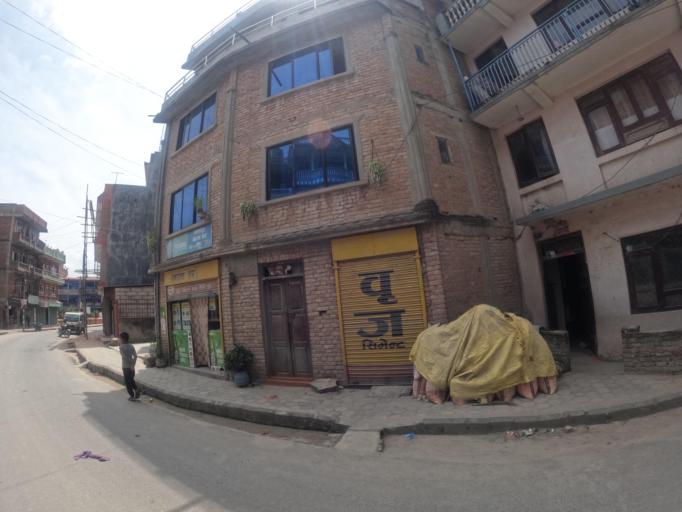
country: NP
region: Central Region
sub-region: Bagmati Zone
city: Bhaktapur
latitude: 27.6843
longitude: 85.3895
